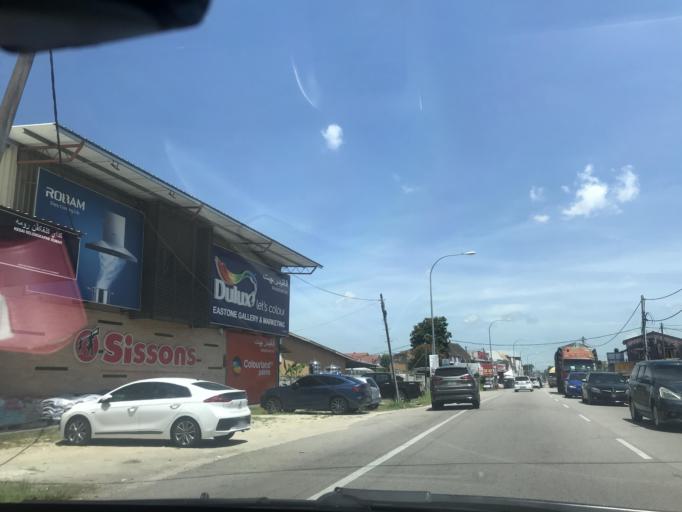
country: MY
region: Kelantan
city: Kota Bharu
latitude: 6.1243
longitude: 102.2663
